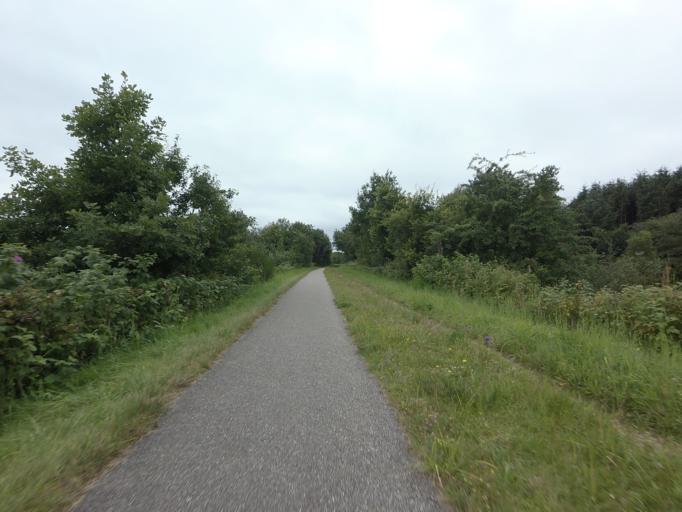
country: DK
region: Central Jutland
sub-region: Silkeborg Kommune
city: Virklund
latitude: 56.0809
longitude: 9.5285
